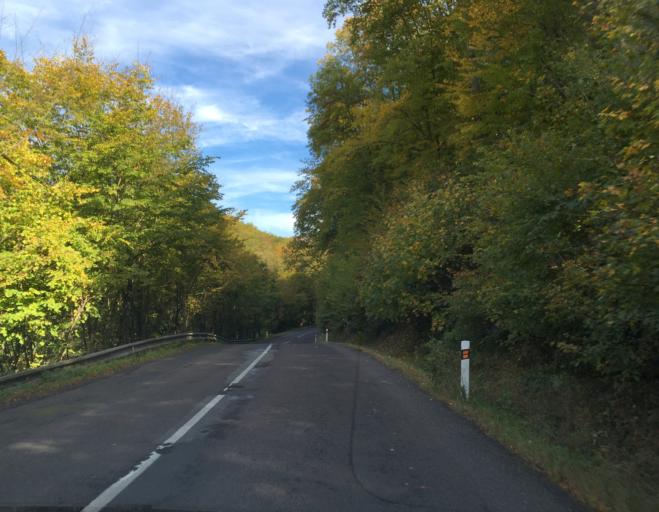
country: SK
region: Banskobystricky
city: Krupina
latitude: 48.3115
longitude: 18.9733
